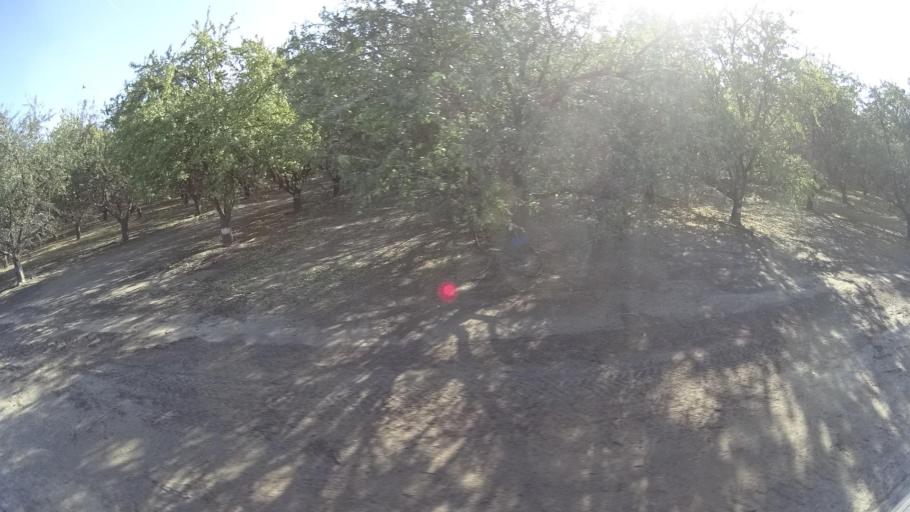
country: US
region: California
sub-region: Kern County
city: McFarland
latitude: 35.7032
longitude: -119.3108
